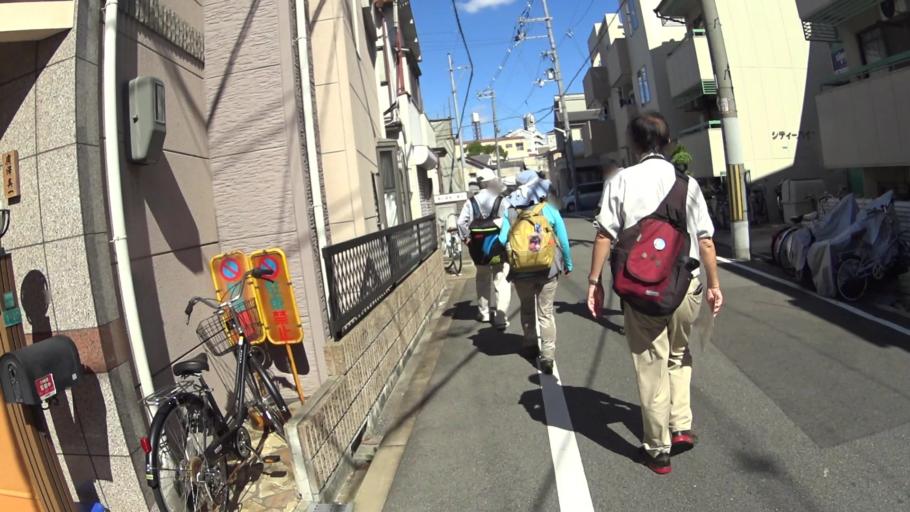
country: JP
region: Osaka
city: Yao
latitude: 34.6278
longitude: 135.5565
